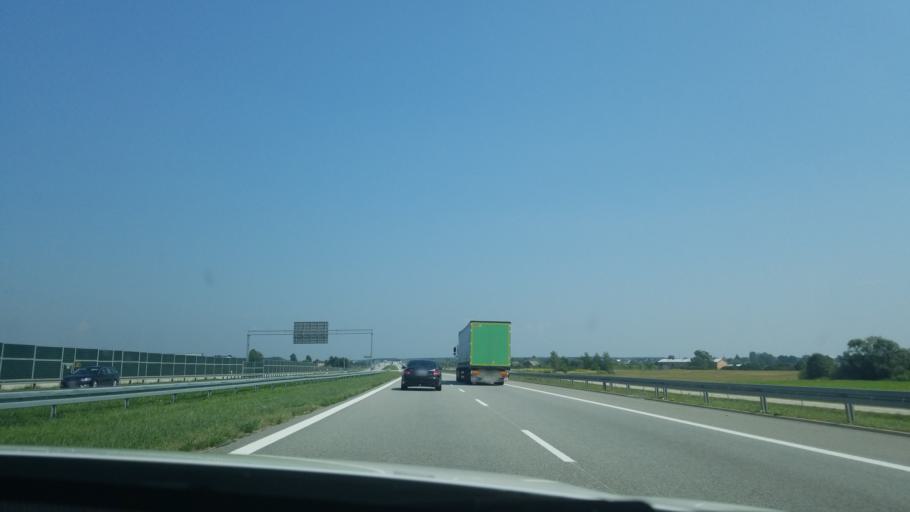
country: PL
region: Subcarpathian Voivodeship
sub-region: Powiat debicki
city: Zyrakow
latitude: 50.0812
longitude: 21.4064
